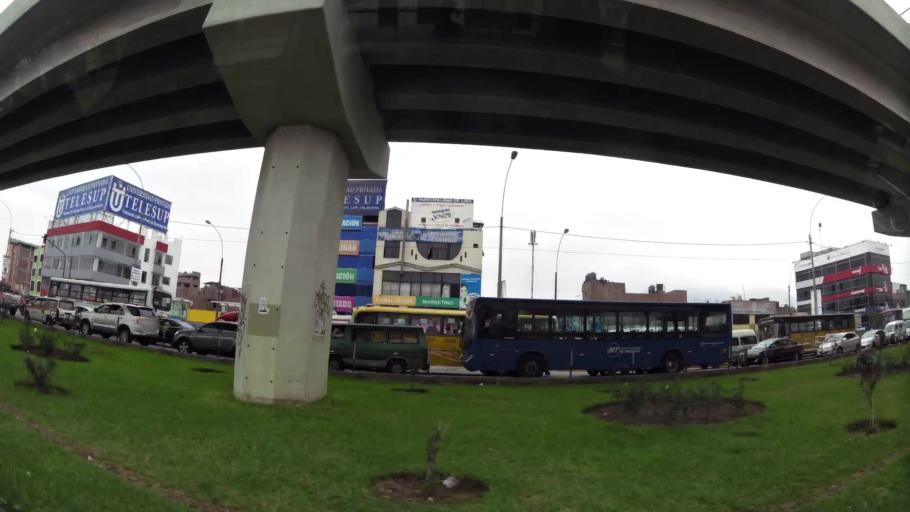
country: PE
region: Lima
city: Lima
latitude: -12.0165
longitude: -77.0015
